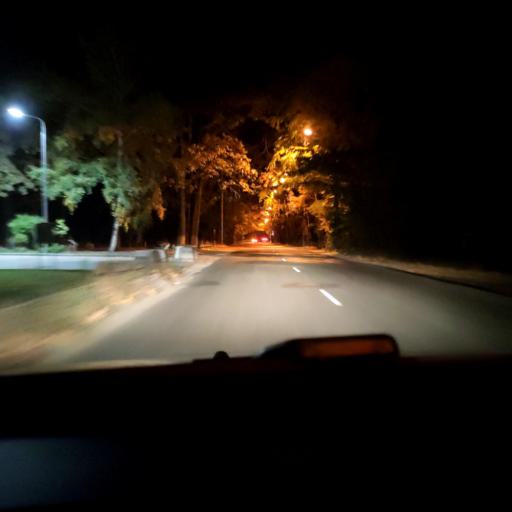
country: RU
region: Voronezj
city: Voronezh
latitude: 51.7209
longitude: 39.2232
